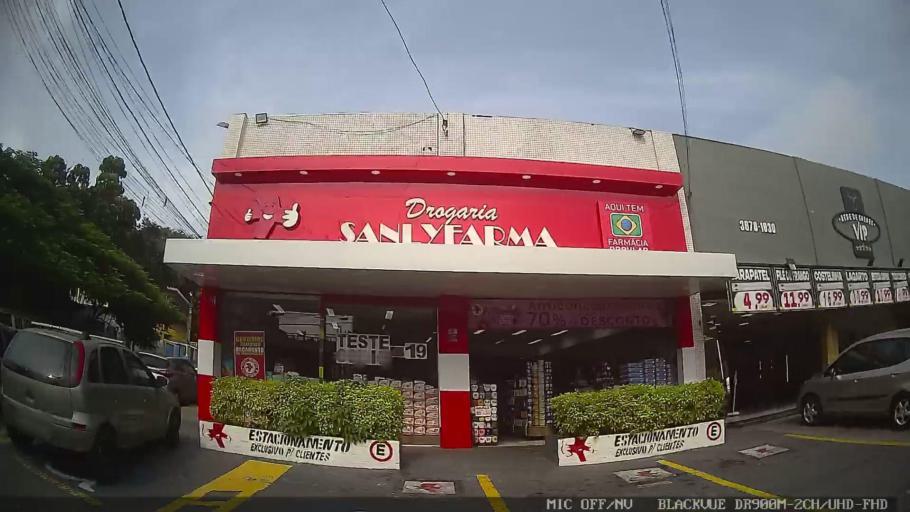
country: BR
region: Sao Paulo
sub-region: Itaquaquecetuba
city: Itaquaquecetuba
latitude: -23.5037
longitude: -46.3669
